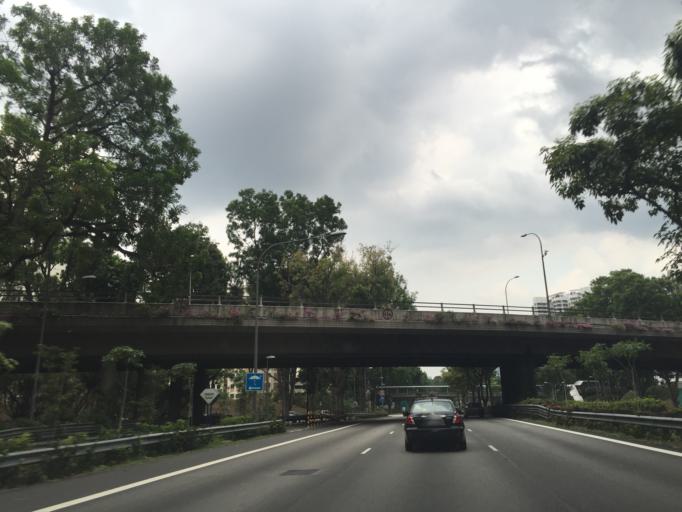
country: SG
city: Singapore
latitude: 1.3150
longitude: 103.7600
